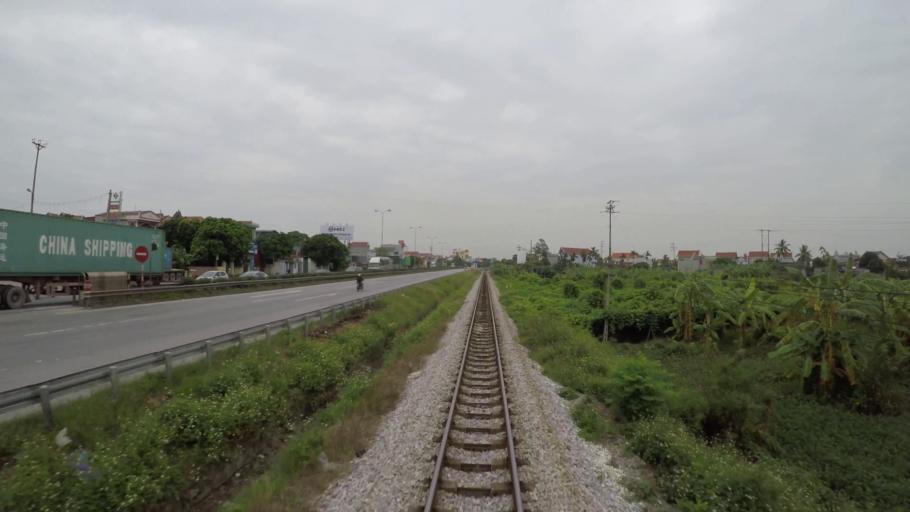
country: VN
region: Hai Duong
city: Phu Thai
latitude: 20.9684
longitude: 106.4557
